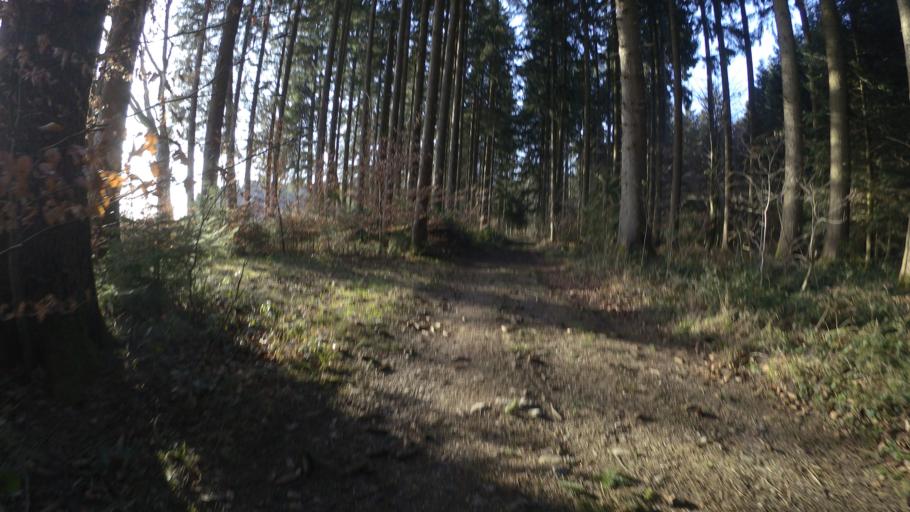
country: DE
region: Bavaria
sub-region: Upper Bavaria
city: Traunreut
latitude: 47.9331
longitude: 12.5762
